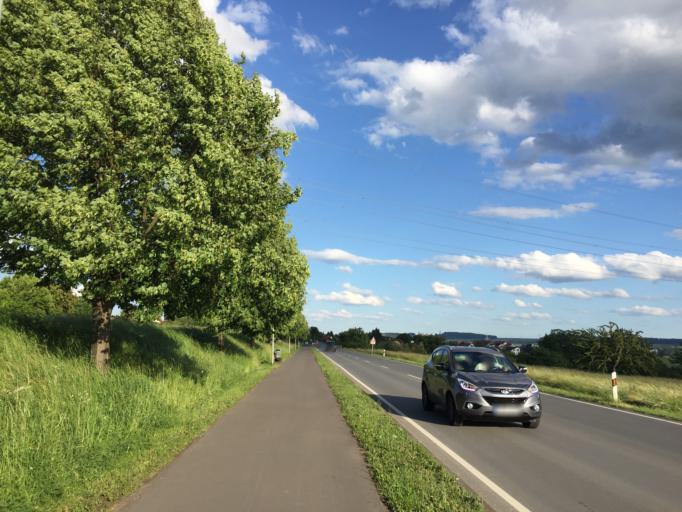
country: DE
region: Hesse
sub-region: Regierungsbezirk Darmstadt
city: Karben
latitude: 50.2177
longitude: 8.7814
